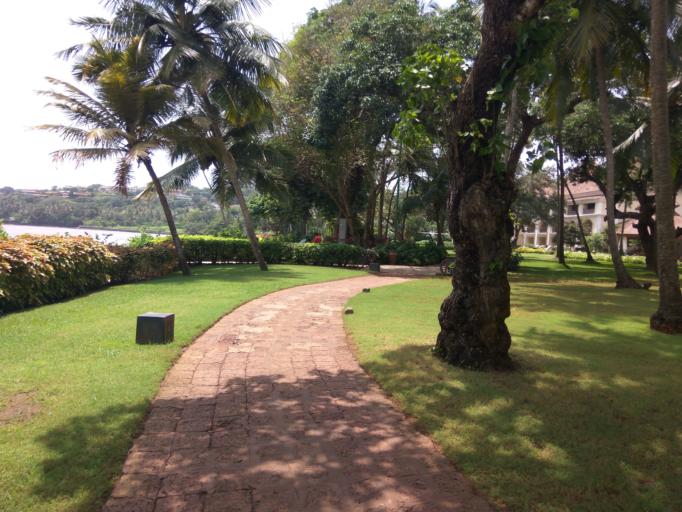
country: IN
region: Goa
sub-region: North Goa
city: Bambolim
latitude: 15.4507
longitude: 73.8511
